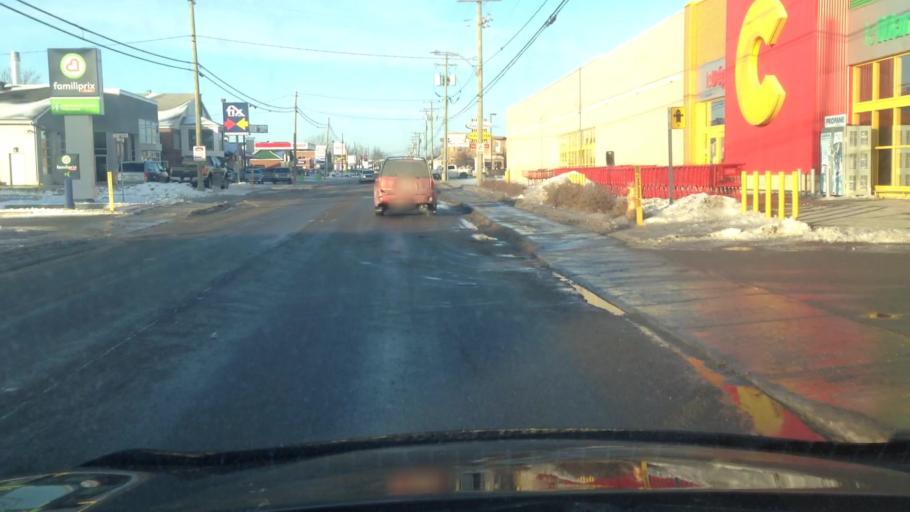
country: CA
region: Quebec
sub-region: Lanaudiere
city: Saint-Lin-Laurentides
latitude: 45.8622
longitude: -73.7571
